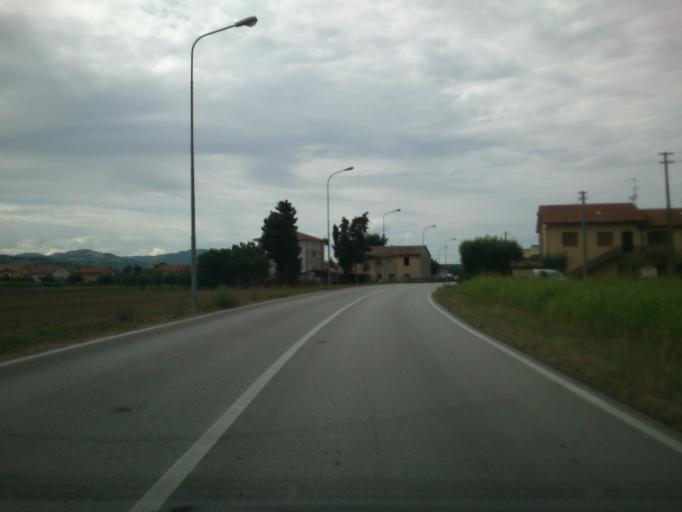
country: IT
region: The Marches
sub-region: Provincia di Pesaro e Urbino
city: Lucrezia
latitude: 43.7718
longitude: 12.9520
